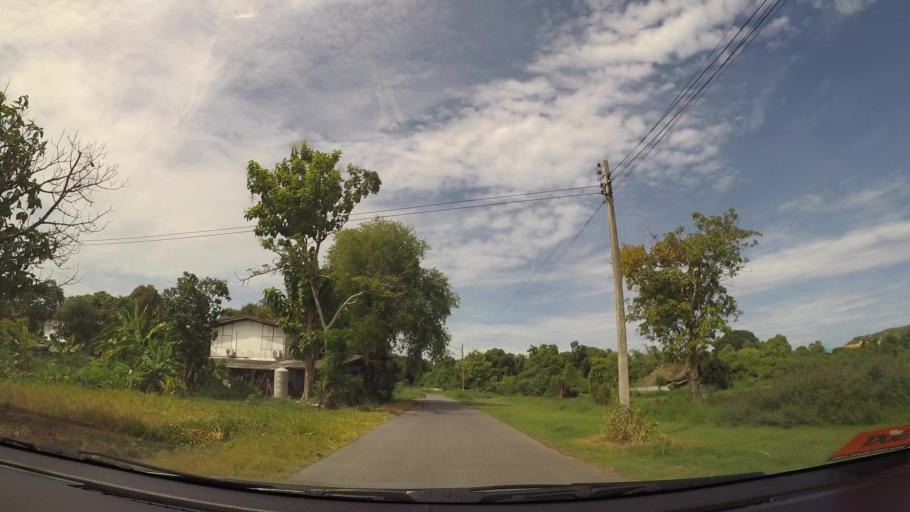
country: TH
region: Chon Buri
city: Sattahip
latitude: 12.6675
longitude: 100.9093
